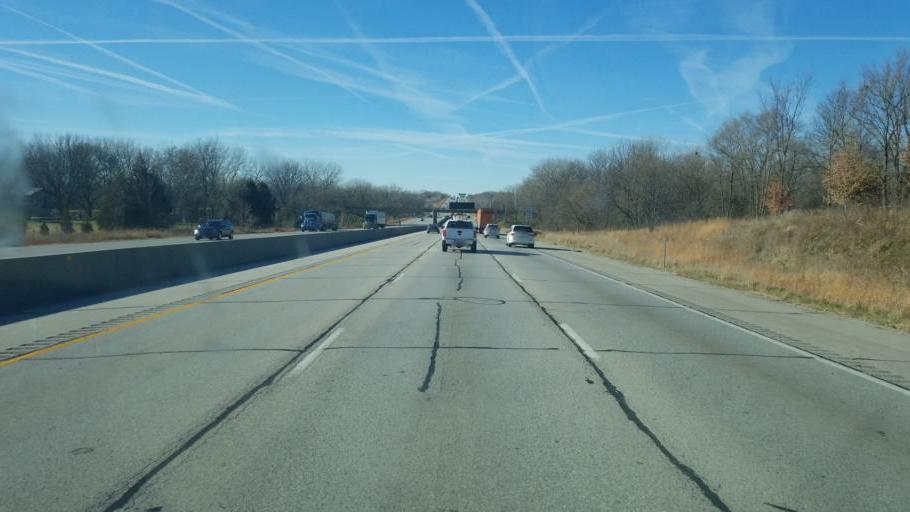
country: US
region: Iowa
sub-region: Polk County
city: Pleasant Hill
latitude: 41.6574
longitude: -93.5400
